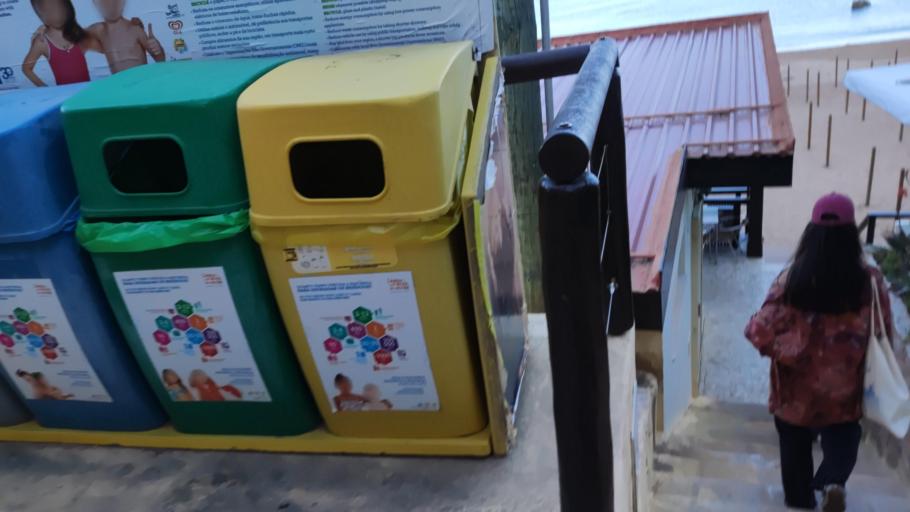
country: PT
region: Faro
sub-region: Lagos
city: Lagos
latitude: 37.0925
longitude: -8.6691
